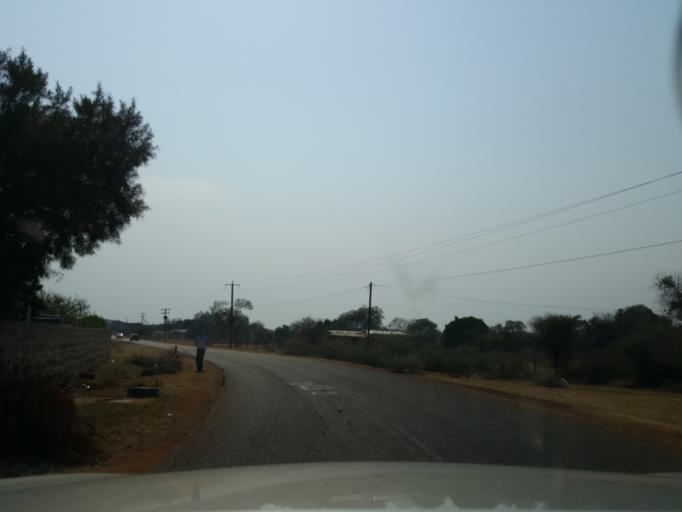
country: BW
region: South East
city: Lobatse
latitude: -25.2888
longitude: 25.9071
